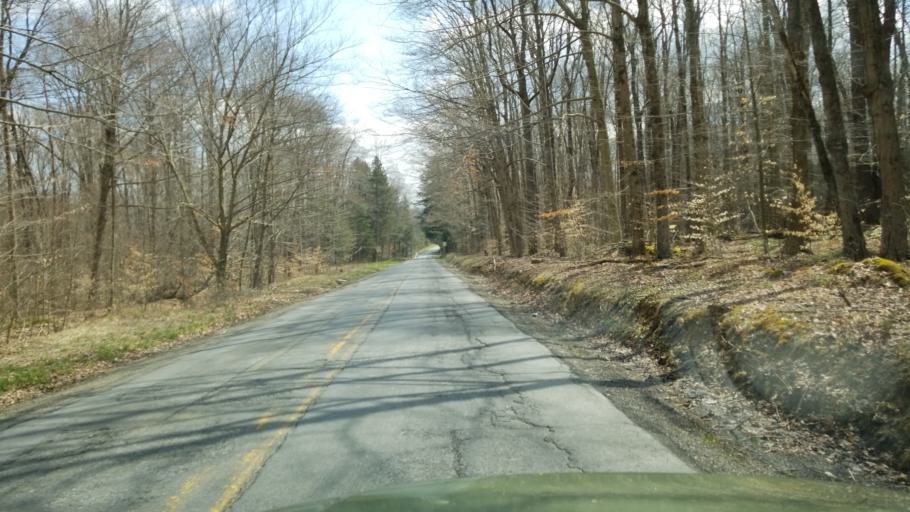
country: US
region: Pennsylvania
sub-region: Jefferson County
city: Brockway
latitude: 41.2787
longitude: -78.8549
